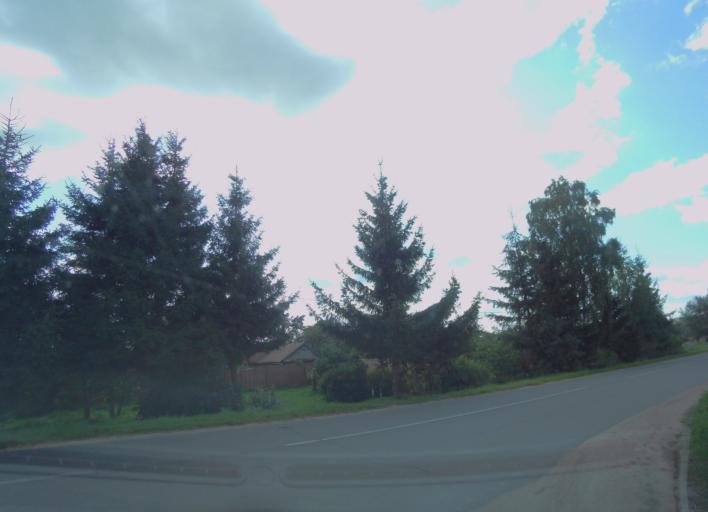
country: BY
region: Minsk
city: Zyembin
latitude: 54.3750
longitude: 28.3812
